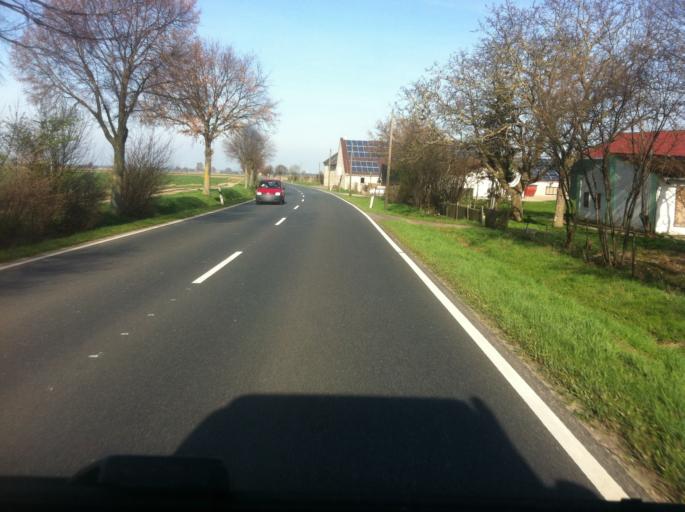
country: DE
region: North Rhine-Westphalia
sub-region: Regierungsbezirk Koln
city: Vettweiss
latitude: 50.7421
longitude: 6.5741
